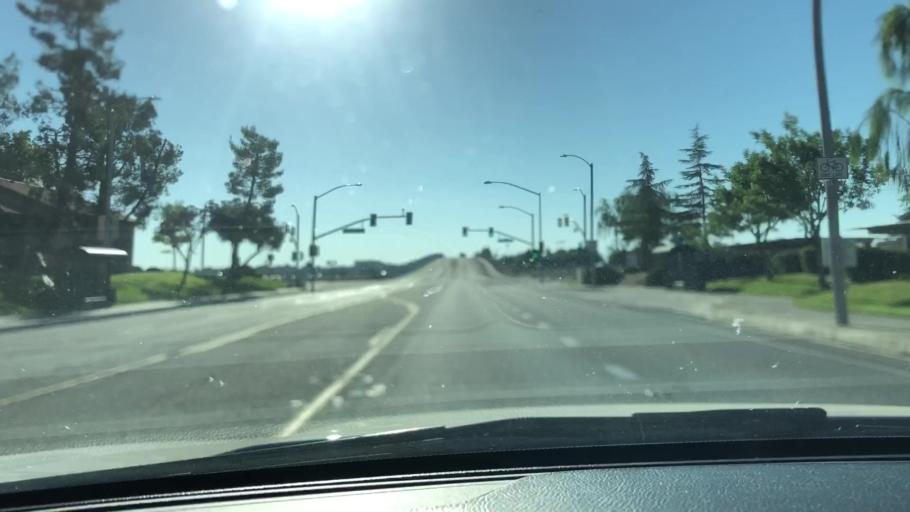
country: US
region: California
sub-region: Los Angeles County
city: Lancaster
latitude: 34.6677
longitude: -118.1577
